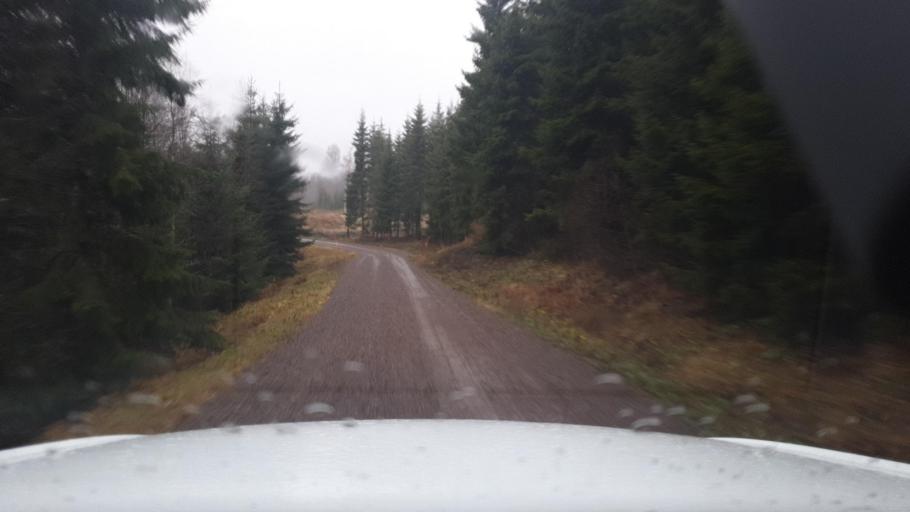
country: SE
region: Vaermland
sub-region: Torsby Kommun
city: Torsby
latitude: 59.9545
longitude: 12.7402
